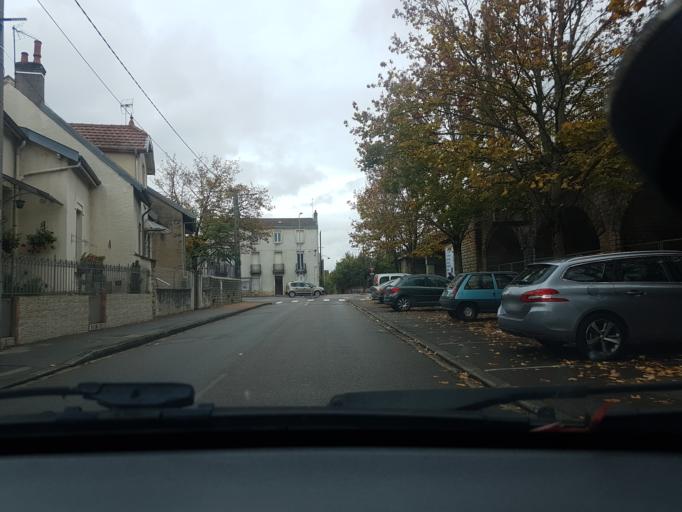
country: FR
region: Bourgogne
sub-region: Departement de la Cote-d'Or
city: Saint-Apollinaire
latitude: 47.3221
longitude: 5.0552
